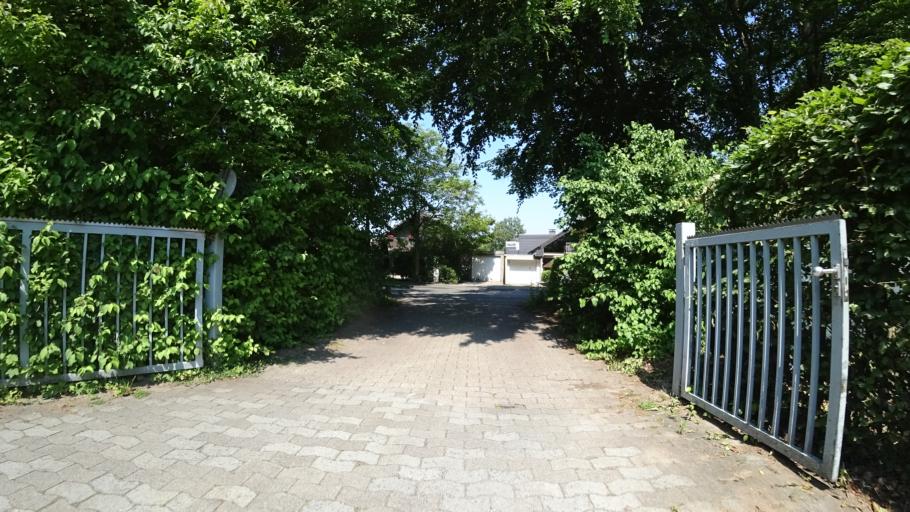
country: DE
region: North Rhine-Westphalia
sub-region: Regierungsbezirk Detmold
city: Guetersloh
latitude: 51.9306
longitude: 8.3655
